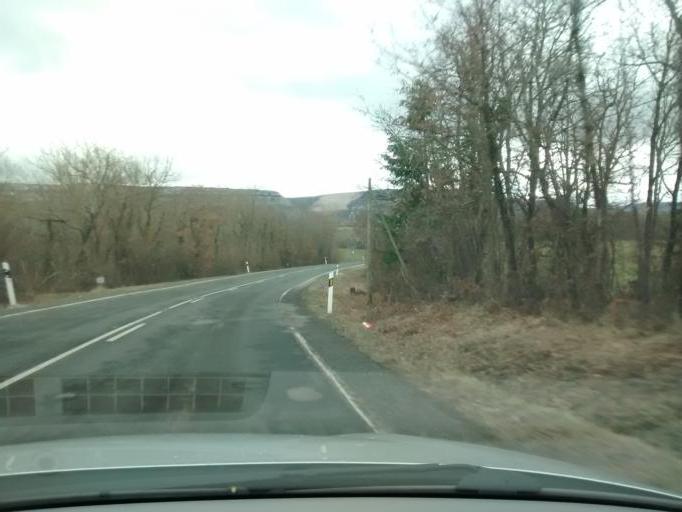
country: ES
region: Castille and Leon
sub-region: Provincia de Burgos
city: Espinosa de los Monteros
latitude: 43.0693
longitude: -3.5122
